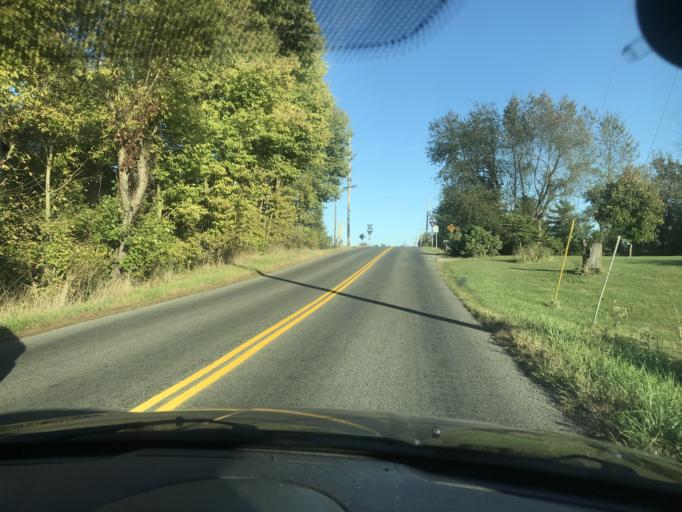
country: US
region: Ohio
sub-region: Logan County
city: Bellefontaine
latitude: 40.3324
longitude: -83.7669
